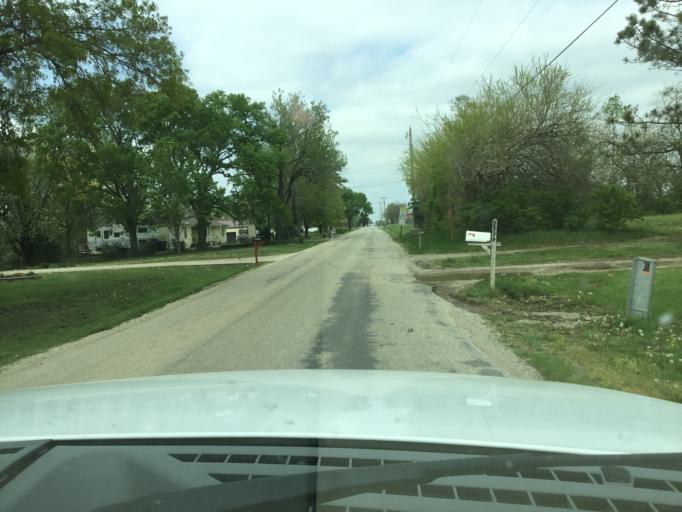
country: US
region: Kansas
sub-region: Shawnee County
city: Topeka
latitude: 39.0037
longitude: -95.5863
